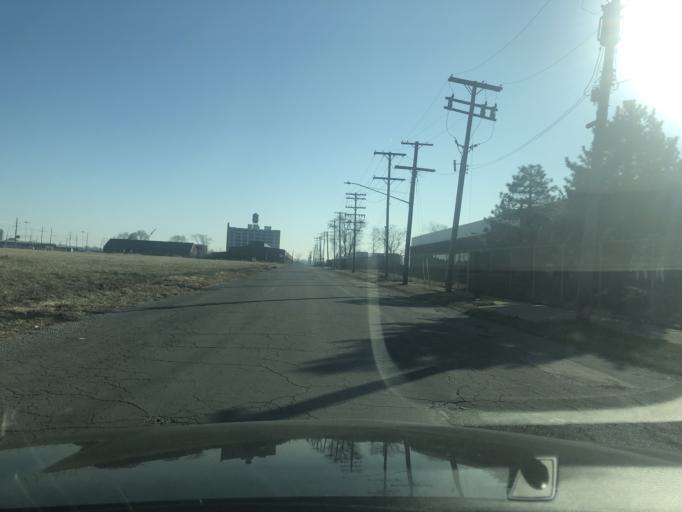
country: US
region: Michigan
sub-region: Wayne County
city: Detroit
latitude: 42.3112
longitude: -83.0910
